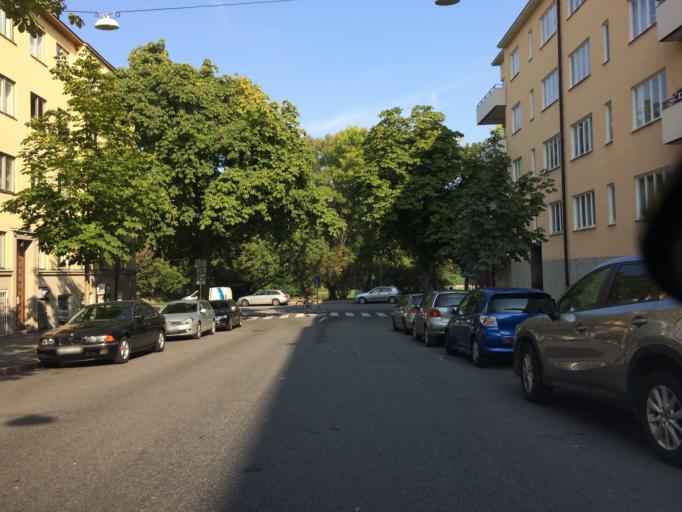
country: SE
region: Stockholm
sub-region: Solna Kommun
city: Solna
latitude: 59.3309
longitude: 18.0032
